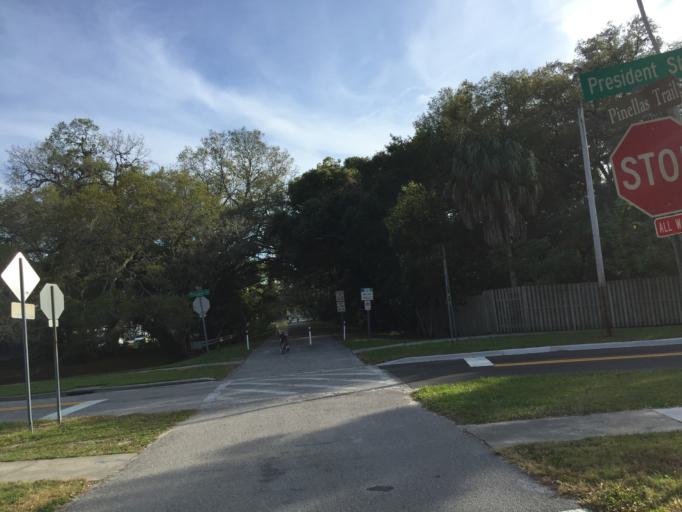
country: US
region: Florida
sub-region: Pinellas County
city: Dunedin
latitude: 28.0085
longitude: -82.7886
